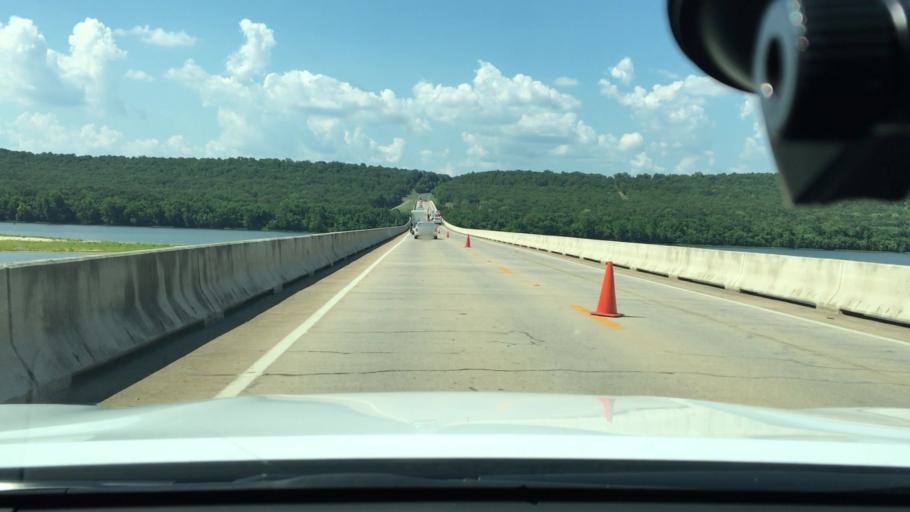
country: US
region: Arkansas
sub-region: Johnson County
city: Clarksville
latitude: 35.4056
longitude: -93.5316
